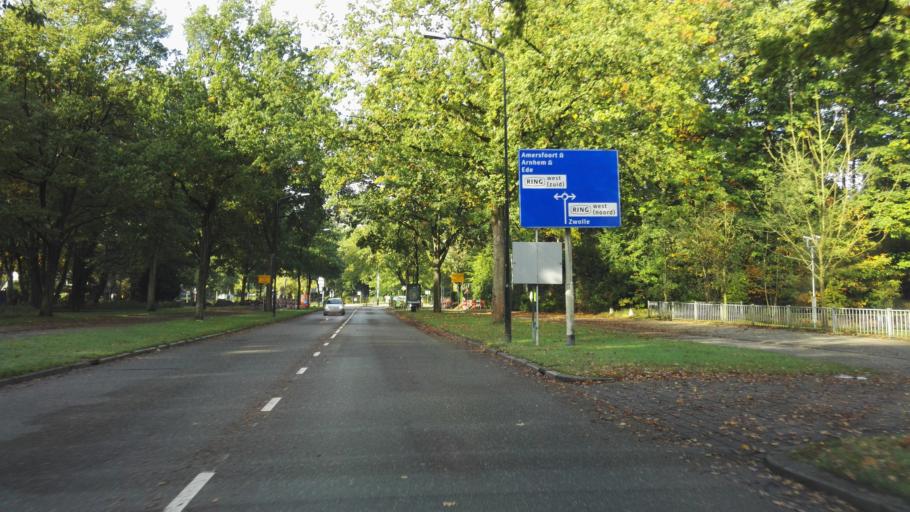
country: NL
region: Gelderland
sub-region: Gemeente Apeldoorn
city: Apeldoorn
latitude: 52.2108
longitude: 5.9336
